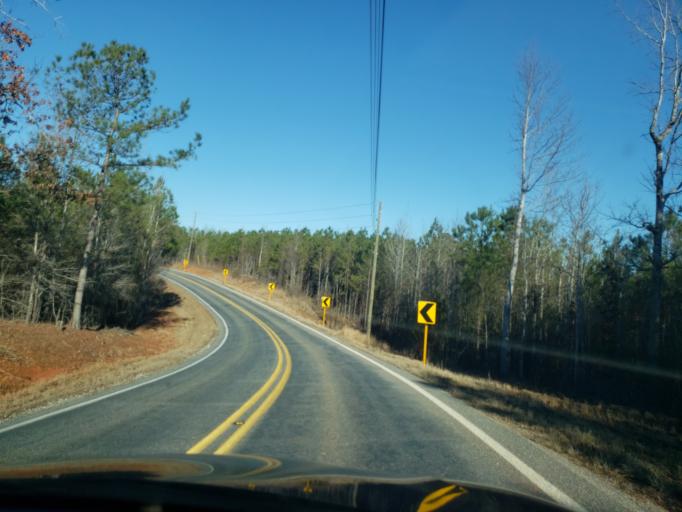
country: US
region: Alabama
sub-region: Elmore County
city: Tallassee
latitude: 32.6728
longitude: -85.8919
